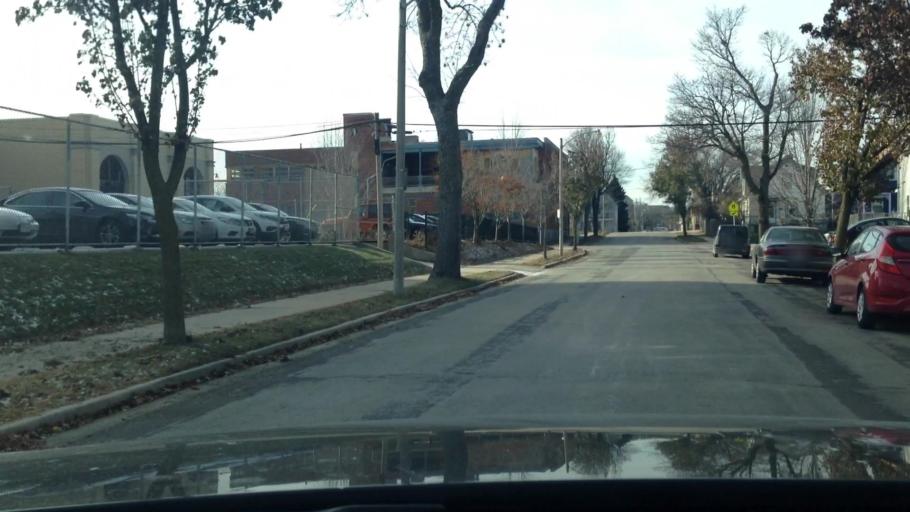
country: US
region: Wisconsin
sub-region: Milwaukee County
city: Shorewood
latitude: 43.0784
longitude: -87.9016
